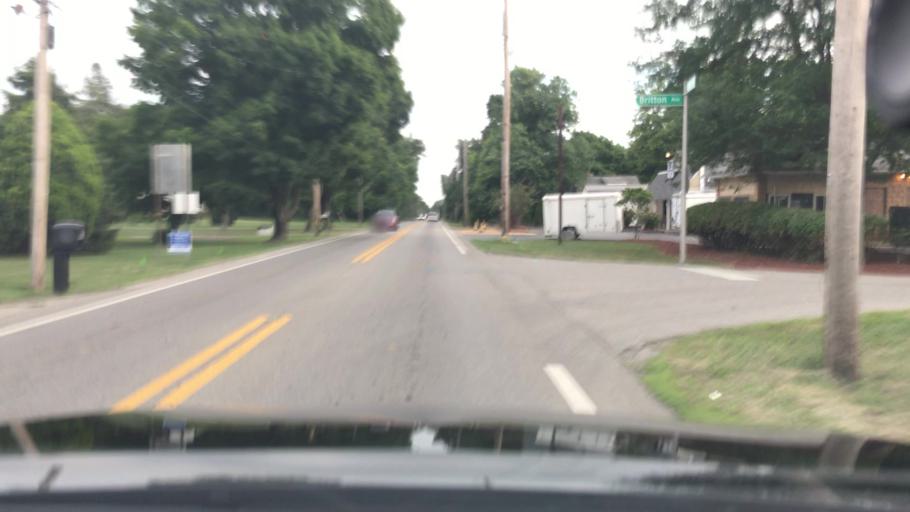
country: US
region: Ohio
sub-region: Franklin County
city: Upper Arlington
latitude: 39.9913
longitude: -83.0922
